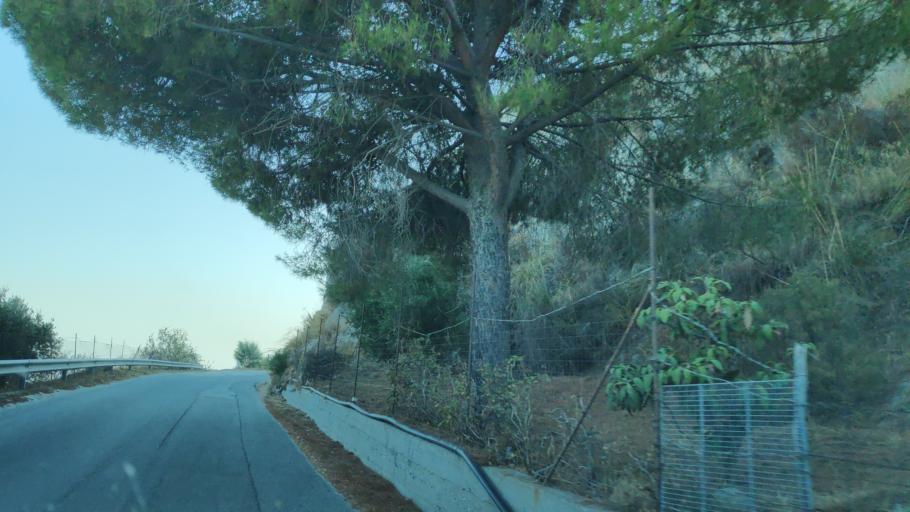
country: IT
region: Calabria
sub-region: Provincia di Reggio Calabria
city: Bova Marina
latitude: 37.9477
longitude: 15.9203
